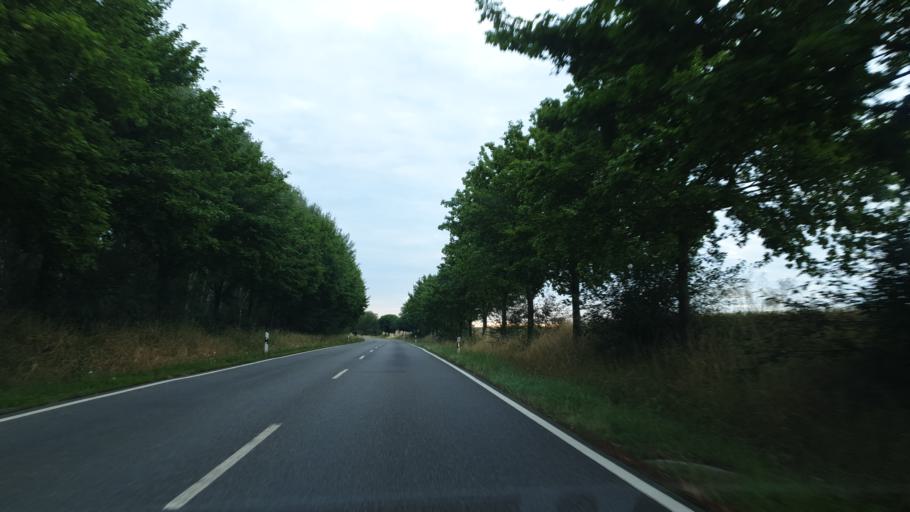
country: DE
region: Saxony
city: Sankt Egidien
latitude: 50.8054
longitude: 12.6284
